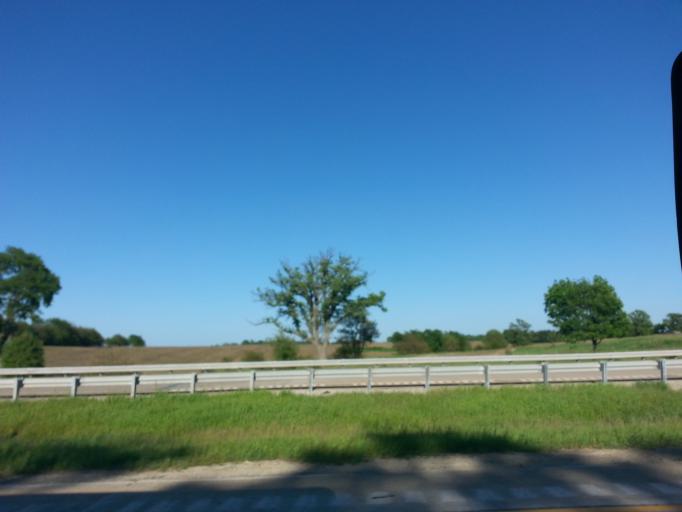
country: US
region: Illinois
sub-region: Woodford County
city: El Paso
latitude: 40.7638
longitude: -89.0348
